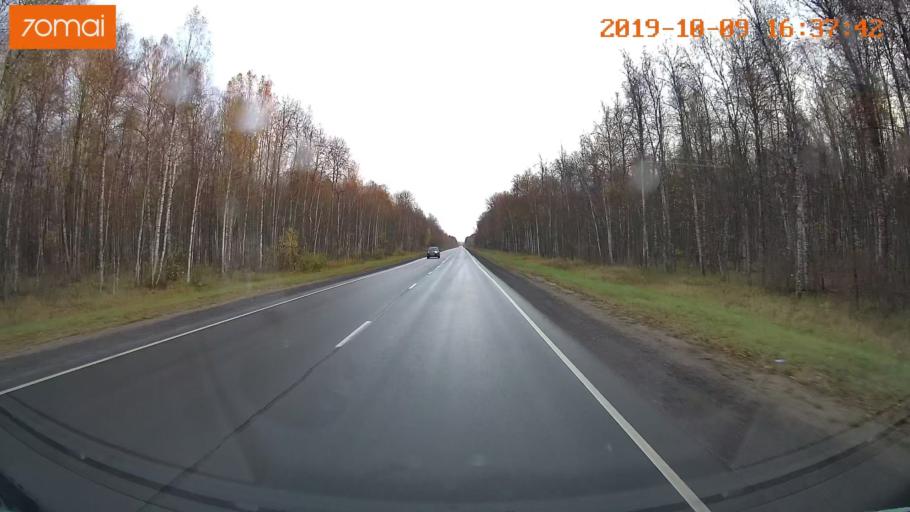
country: RU
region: Kostroma
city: Volgorechensk
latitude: 57.5229
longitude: 41.0280
